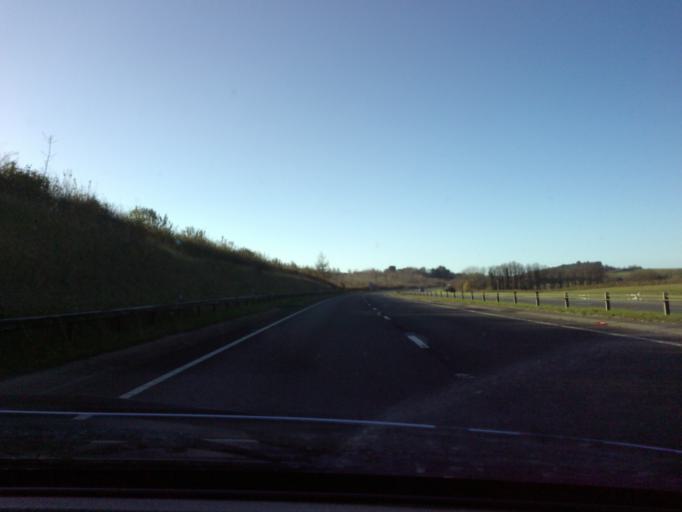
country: GB
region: England
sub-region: Dorset
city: Bovington Camp
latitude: 50.7532
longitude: -2.2502
